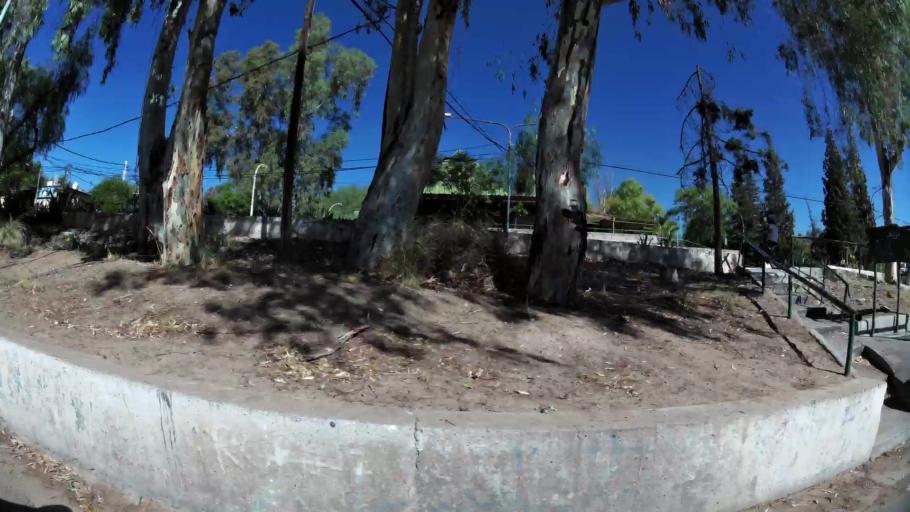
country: AR
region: Mendoza
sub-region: Departamento de Godoy Cruz
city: Godoy Cruz
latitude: -32.9024
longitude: -68.8862
